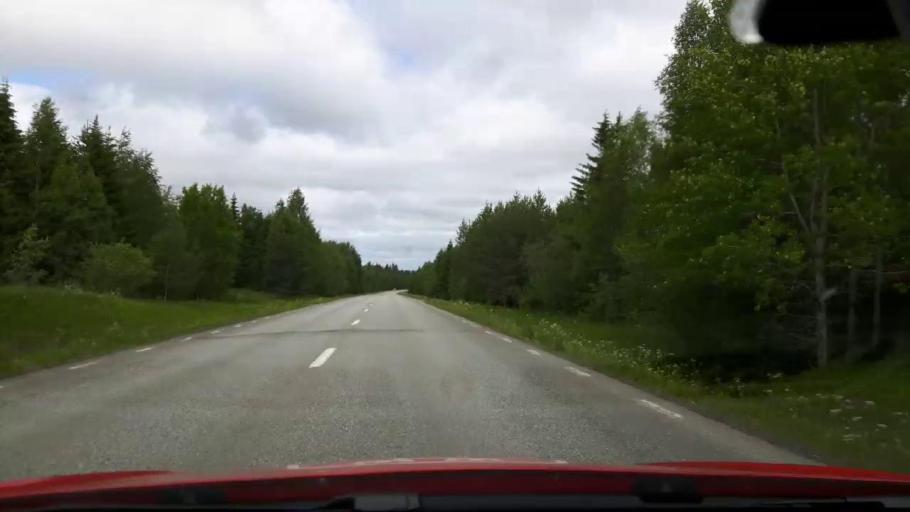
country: SE
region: Jaemtland
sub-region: Krokoms Kommun
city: Krokom
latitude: 63.3713
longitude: 14.5073
